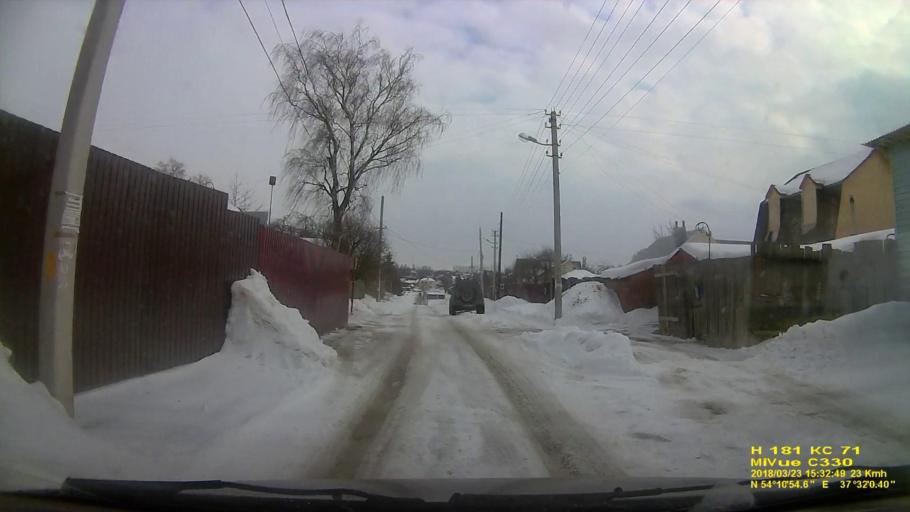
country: RU
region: Tula
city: Kosaya Gora
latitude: 54.1818
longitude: 37.5335
